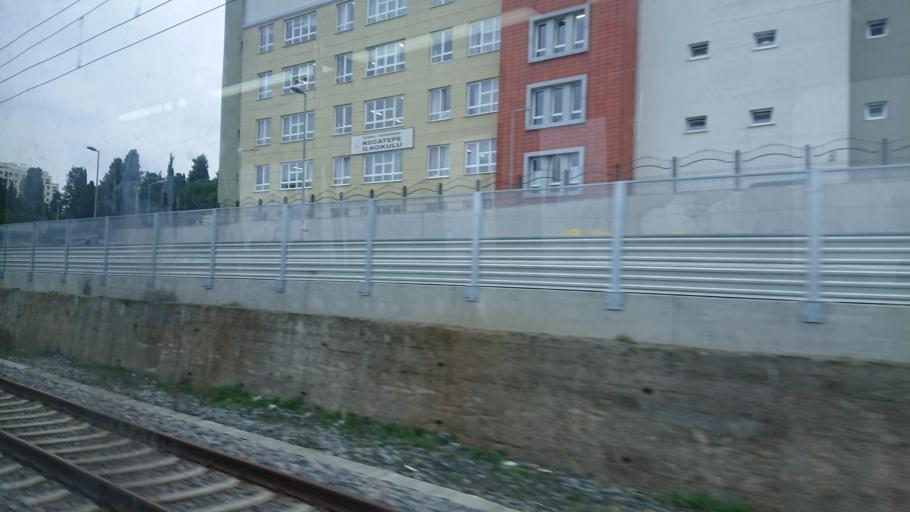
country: TR
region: Istanbul
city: Mahmutbey
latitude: 41.0024
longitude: 28.7698
